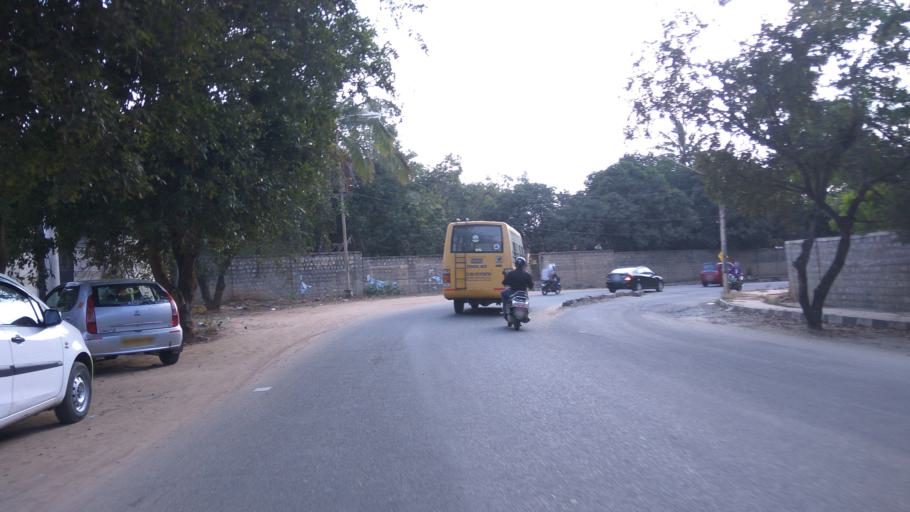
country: IN
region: Karnataka
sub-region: Bangalore Urban
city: Bangalore
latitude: 12.9642
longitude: 77.6919
